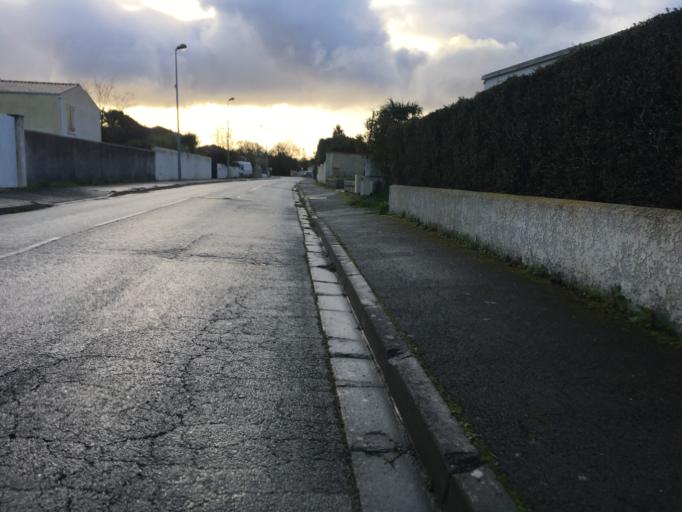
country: FR
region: Poitou-Charentes
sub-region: Departement de la Charente-Maritime
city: Nieul-sur-Mer
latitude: 46.1912
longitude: -1.1854
